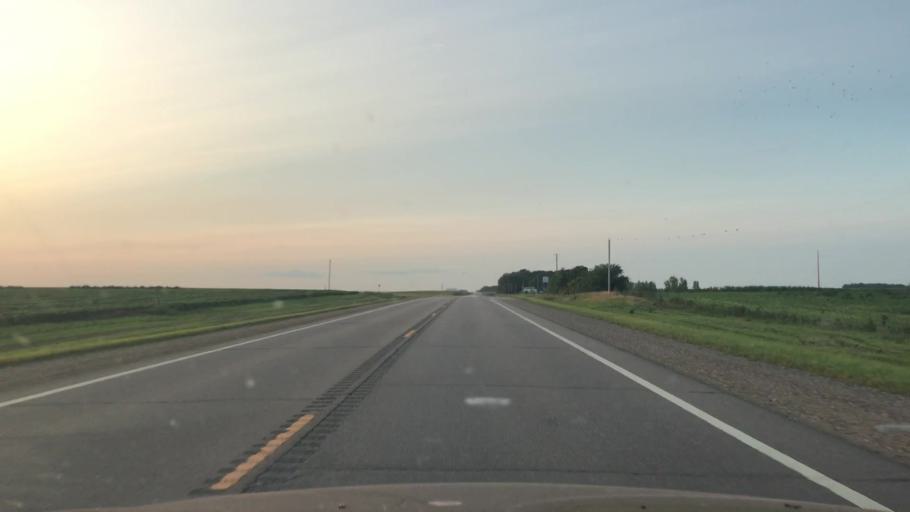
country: US
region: Minnesota
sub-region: Redwood County
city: Redwood Falls
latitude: 44.4396
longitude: -95.1177
